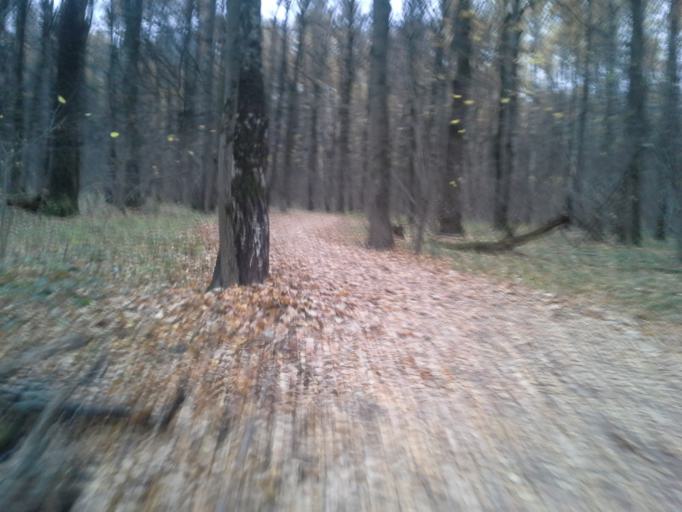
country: RU
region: Moscow
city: Chertanovo Yuzhnoye
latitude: 55.6198
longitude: 37.5751
